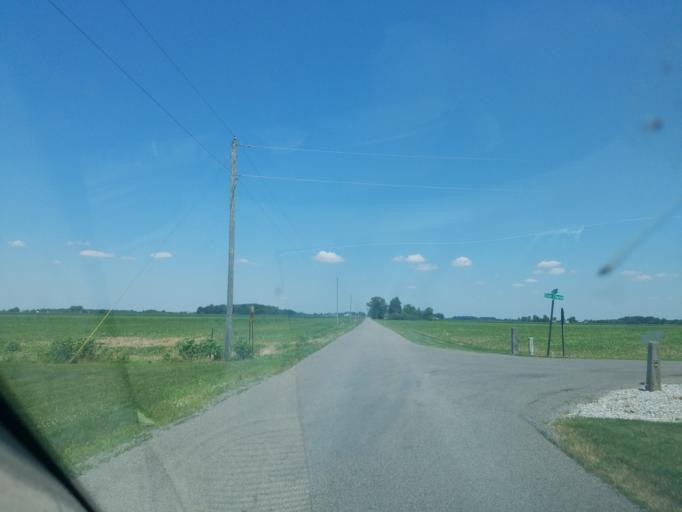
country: US
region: Ohio
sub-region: Allen County
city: Spencerville
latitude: 40.7647
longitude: -84.3496
